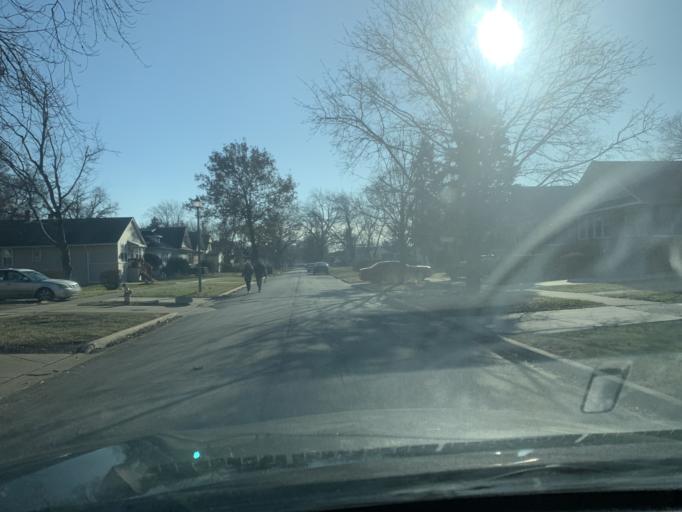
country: US
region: Illinois
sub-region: Cook County
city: Maywood
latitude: 41.8692
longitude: -87.8361
